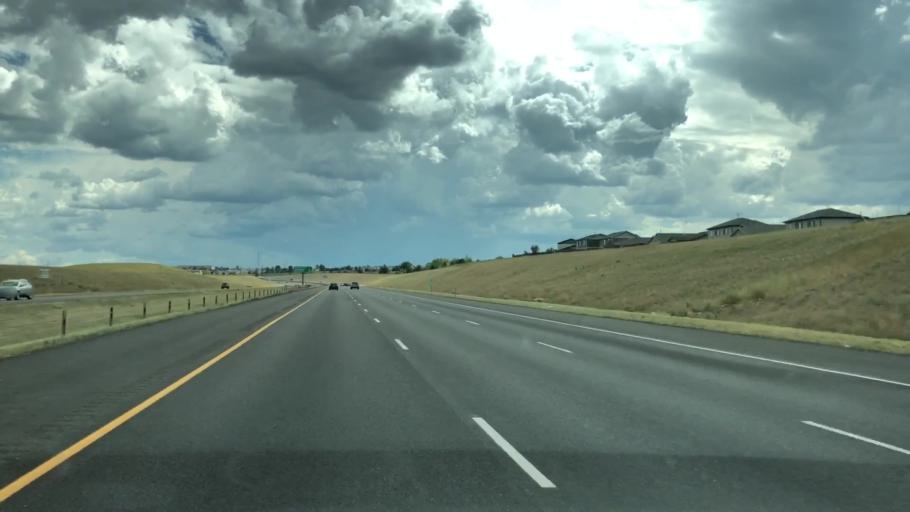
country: US
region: Colorado
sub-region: Douglas County
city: Parker
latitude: 39.6268
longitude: -104.7192
